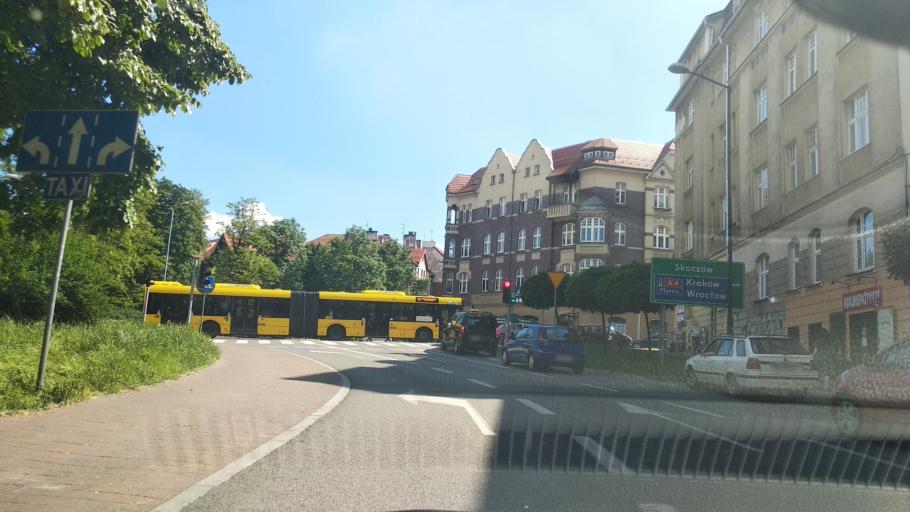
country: PL
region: Silesian Voivodeship
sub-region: Katowice
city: Katowice
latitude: 50.2524
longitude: 19.0075
